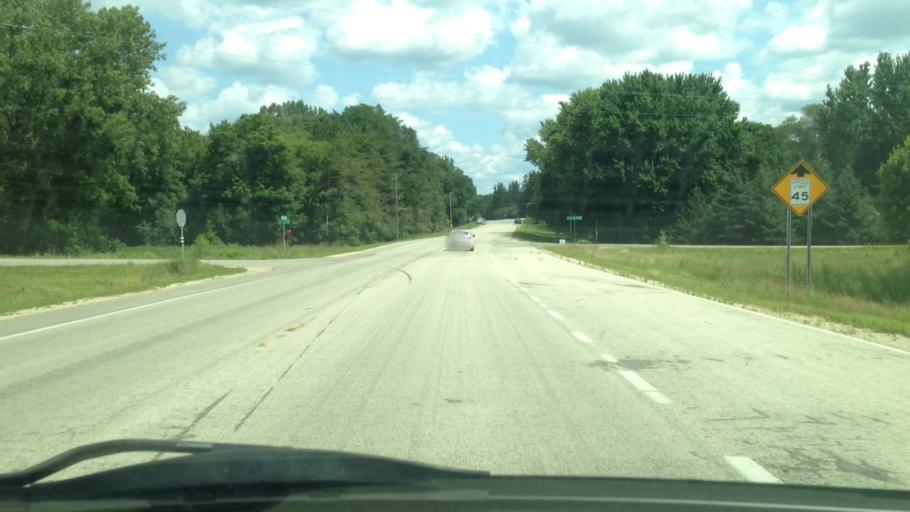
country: US
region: Minnesota
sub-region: Olmsted County
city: Rochester
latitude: 43.9876
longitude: -92.5042
